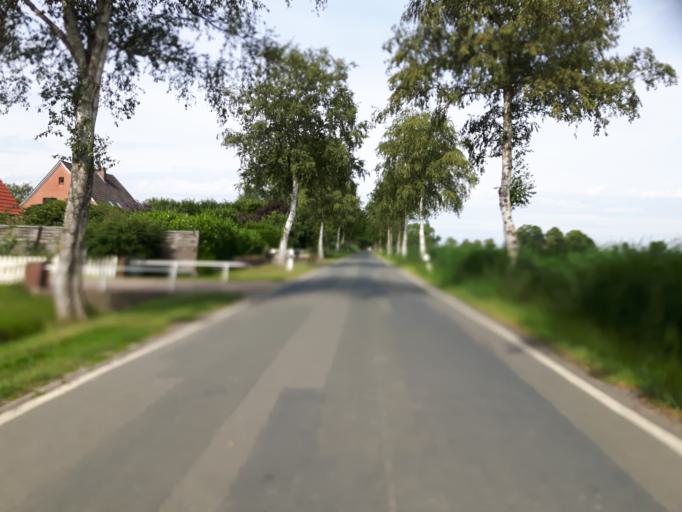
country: DE
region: Lower Saxony
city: Elsfleth
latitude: 53.2581
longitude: 8.4448
